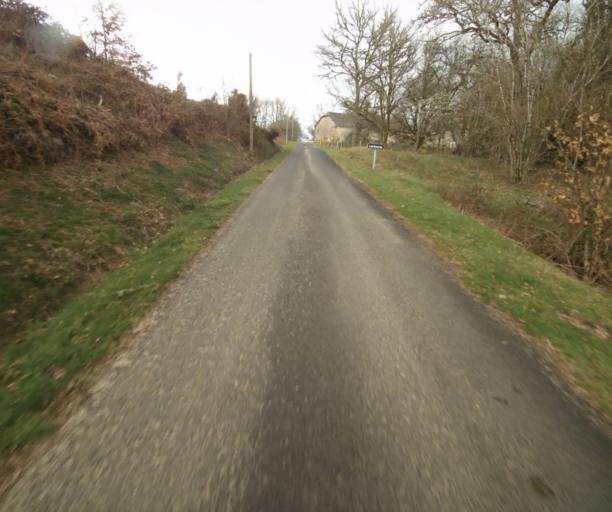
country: FR
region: Limousin
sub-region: Departement de la Correze
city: Egletons
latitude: 45.2694
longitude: 1.9933
